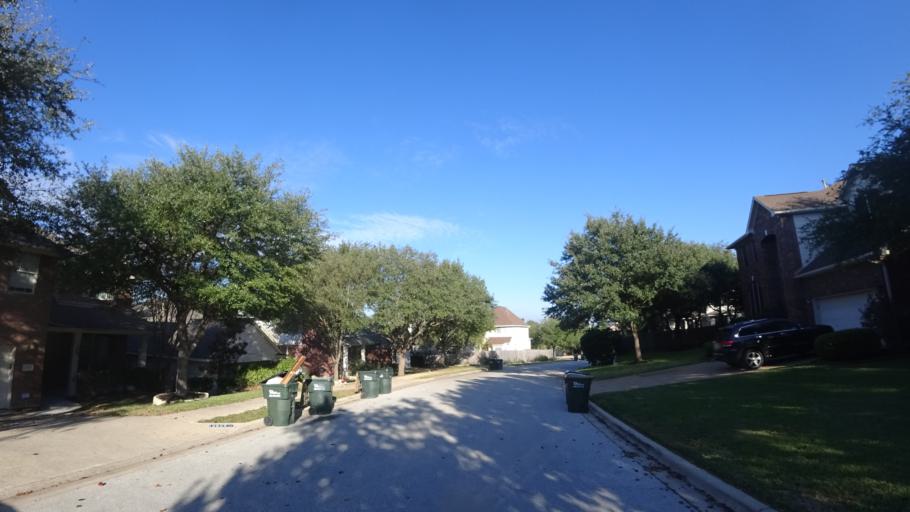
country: US
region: Texas
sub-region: Travis County
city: Hudson Bend
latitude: 30.3712
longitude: -97.8999
